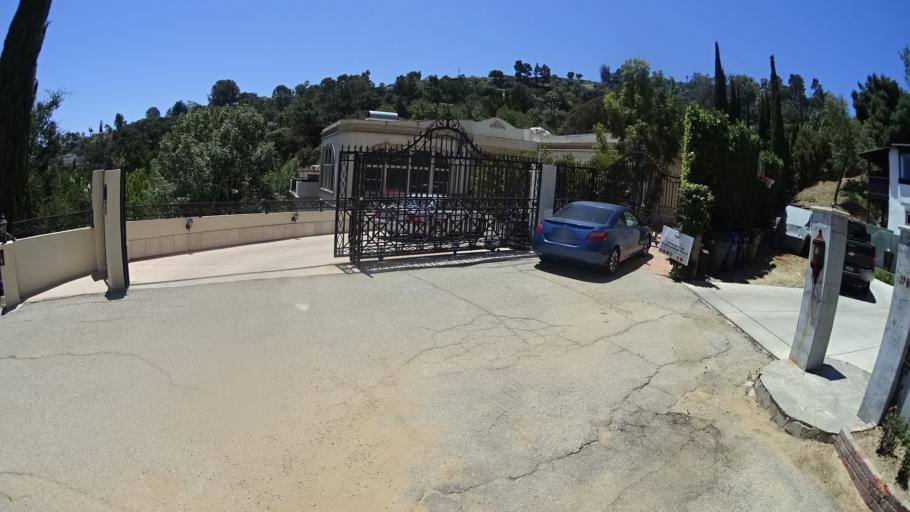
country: US
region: California
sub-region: Los Angeles County
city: Universal City
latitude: 34.1316
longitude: -118.3591
